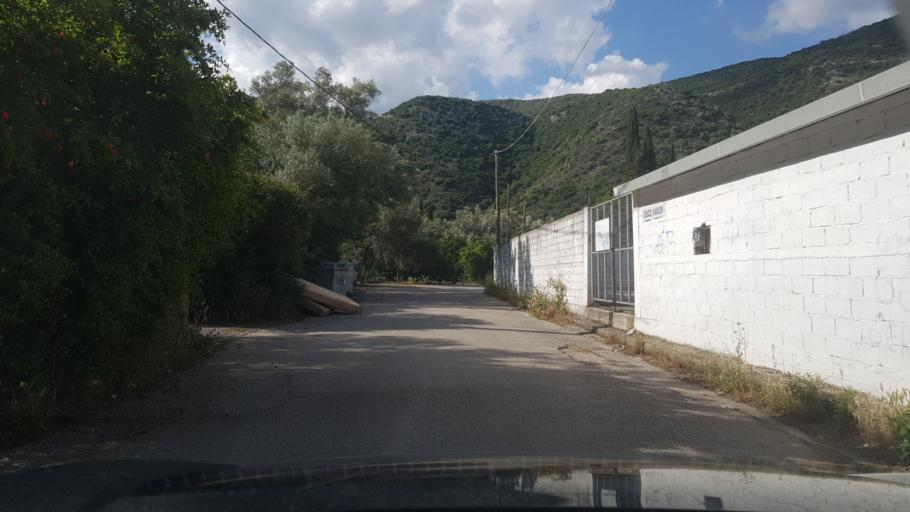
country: GR
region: Ionian Islands
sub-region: Lefkada
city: Nidri
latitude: 38.7183
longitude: 20.6950
